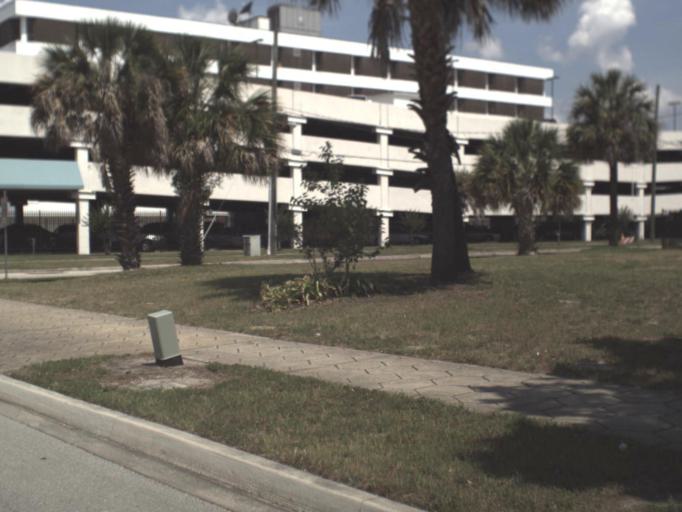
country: US
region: Florida
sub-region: Duval County
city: Jacksonville
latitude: 30.3462
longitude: -81.6598
